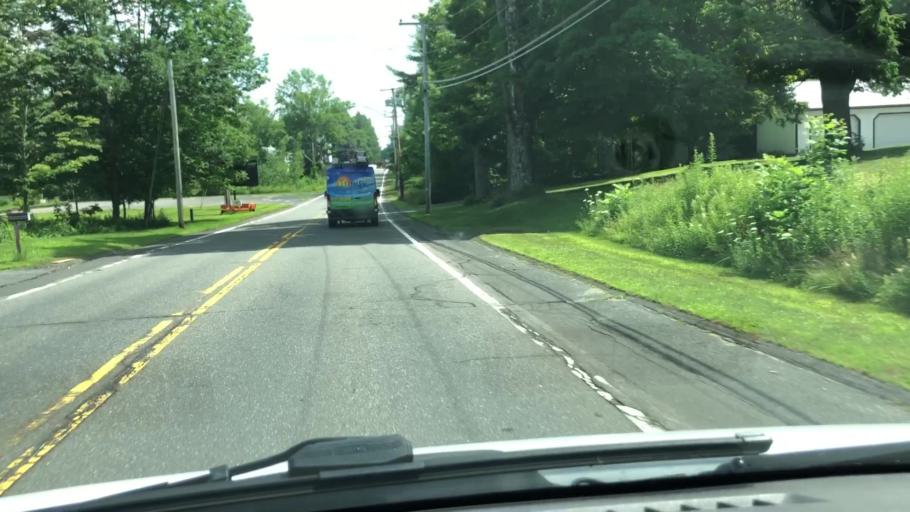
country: US
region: Massachusetts
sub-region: Hampshire County
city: Chesterfield
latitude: 42.4437
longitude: -72.8011
